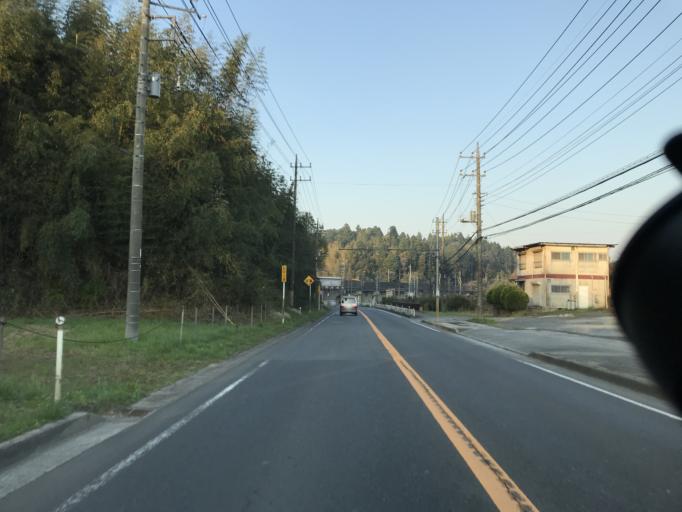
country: JP
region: Chiba
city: Narita
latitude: 35.7964
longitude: 140.3403
